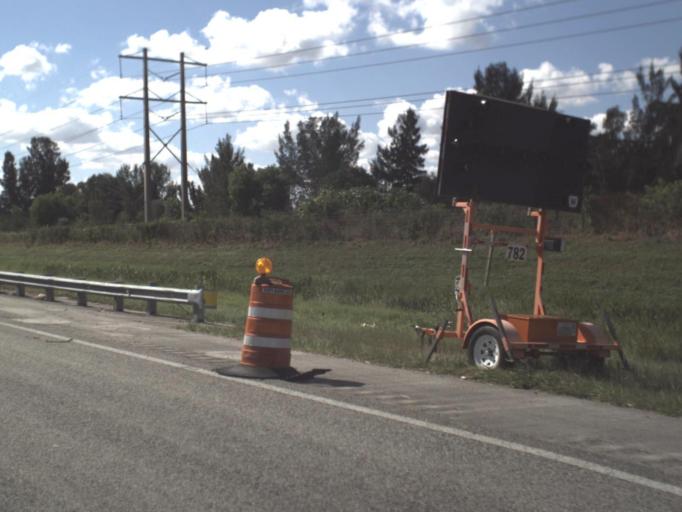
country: US
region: Florida
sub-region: Broward County
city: Pine Island Ridge
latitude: 26.1622
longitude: -80.3267
